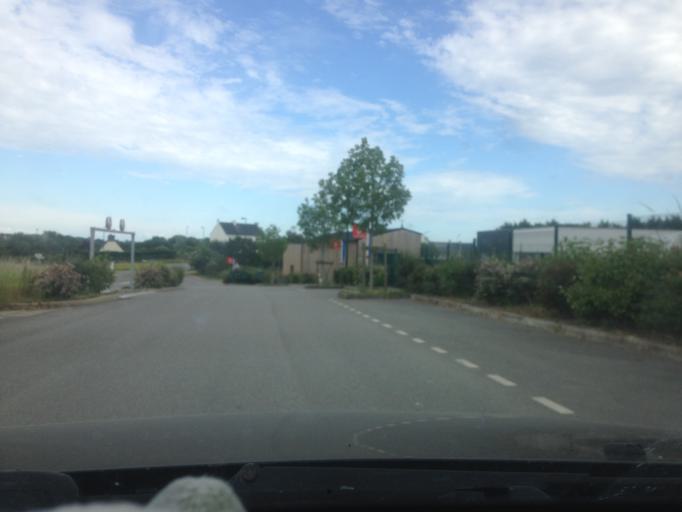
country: FR
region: Brittany
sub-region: Departement du Morbihan
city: Carnac
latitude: 47.5883
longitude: -3.0610
